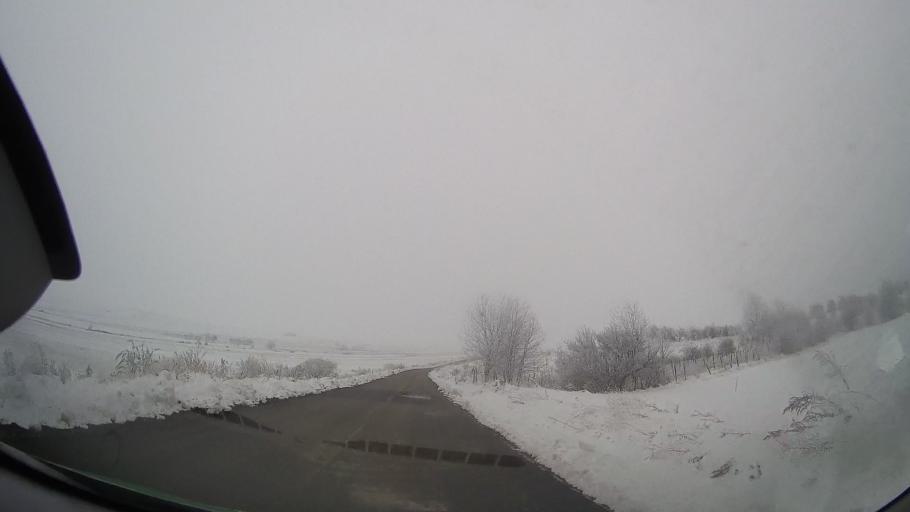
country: RO
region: Iasi
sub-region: Comuna Tansa
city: Suhulet
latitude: 46.8876
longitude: 27.2770
